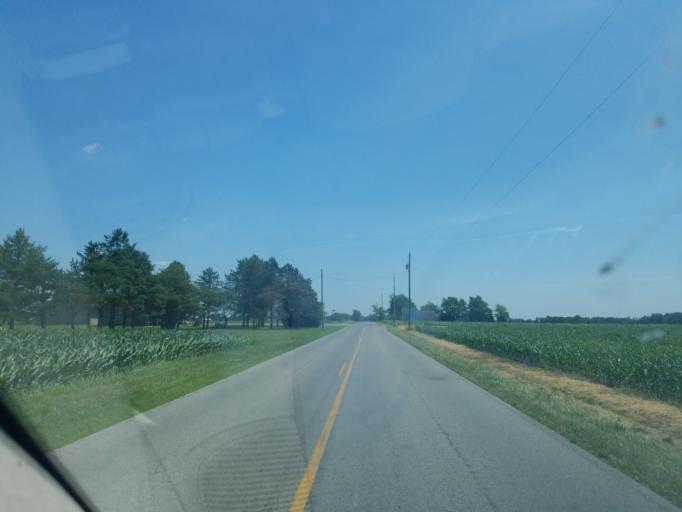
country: US
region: Ohio
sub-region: Allen County
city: Elida
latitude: 40.7872
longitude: -84.2588
